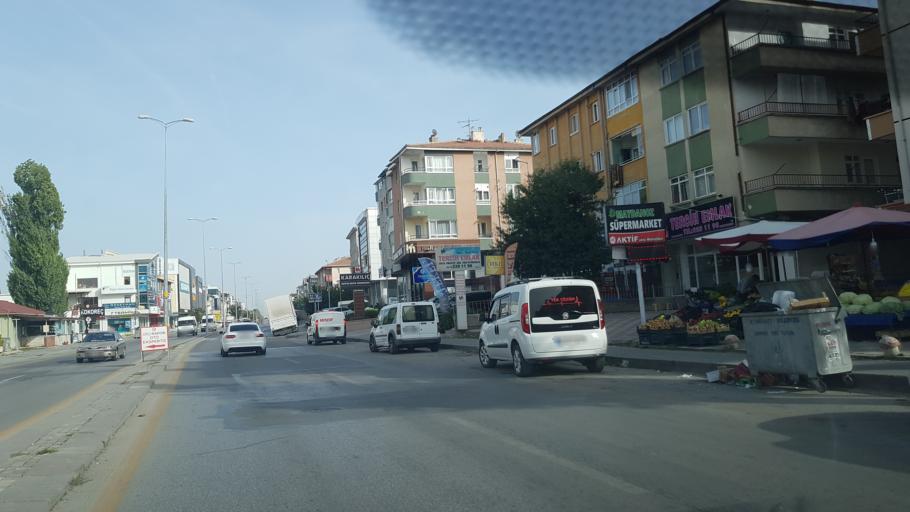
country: TR
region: Ankara
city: Etimesgut
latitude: 39.9509
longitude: 32.6502
